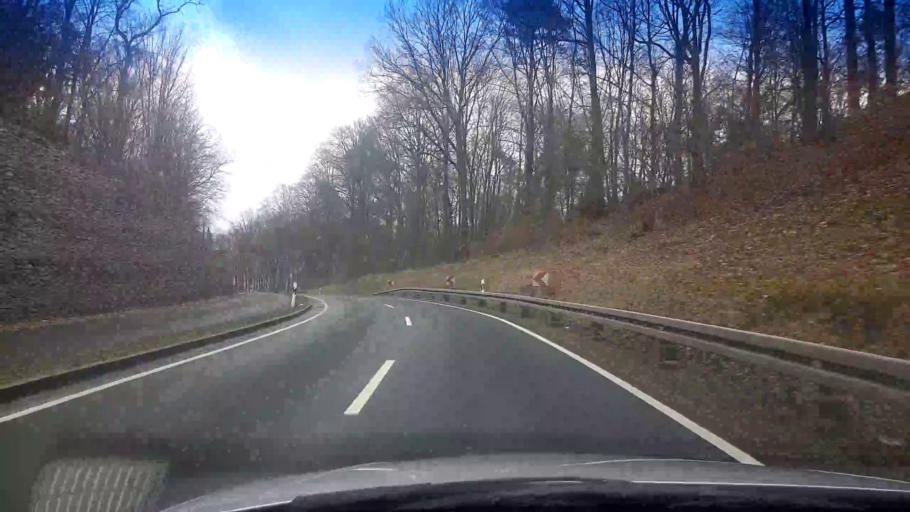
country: DE
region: Bavaria
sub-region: Regierungsbezirk Unterfranken
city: Sand
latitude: 49.9563
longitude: 10.5788
